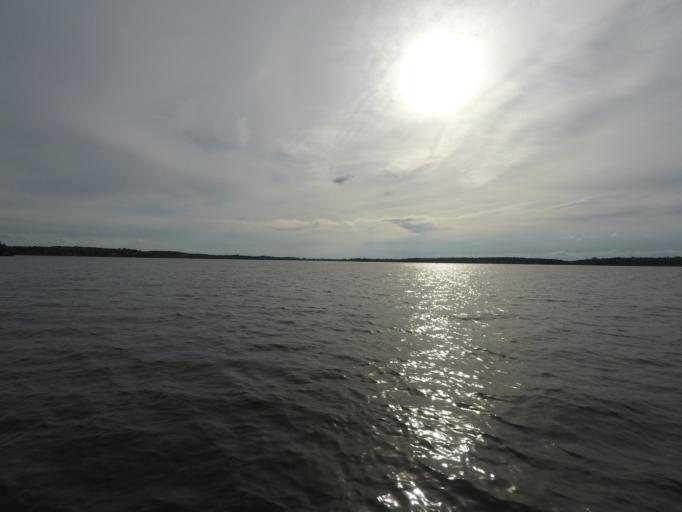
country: SE
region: Soedermanland
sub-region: Eskilstuna Kommun
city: Kvicksund
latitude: 59.4649
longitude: 16.3685
